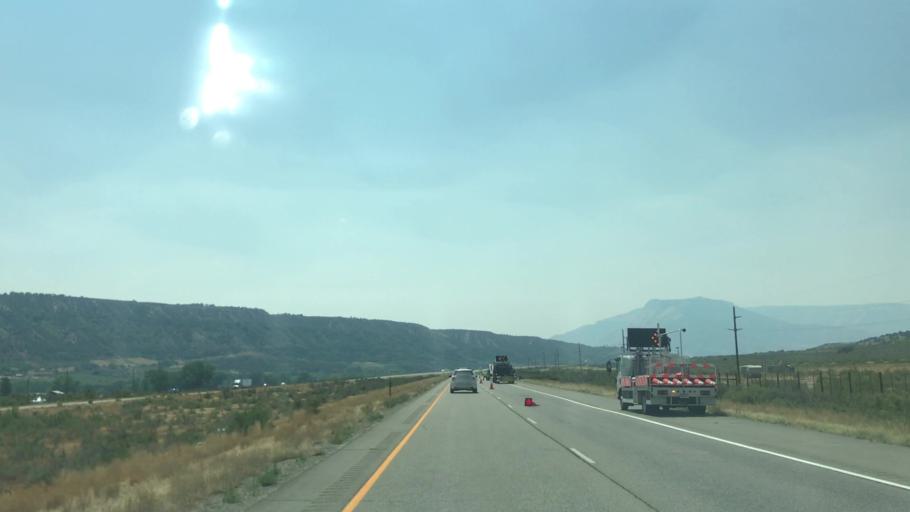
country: US
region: Colorado
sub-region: Garfield County
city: Battlement Mesa
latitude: 39.4829
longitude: -107.9671
